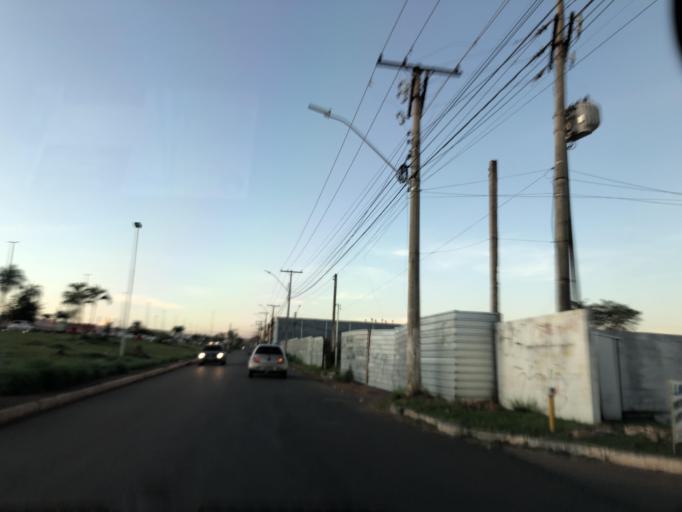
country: BR
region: Goias
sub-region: Luziania
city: Luziania
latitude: -16.0633
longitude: -47.9832
